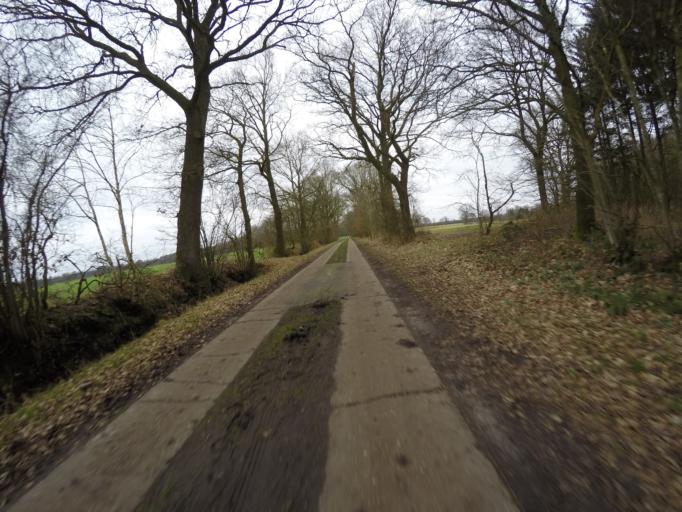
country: DE
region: Schleswig-Holstein
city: Hemdingen
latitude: 53.7771
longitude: 9.8410
